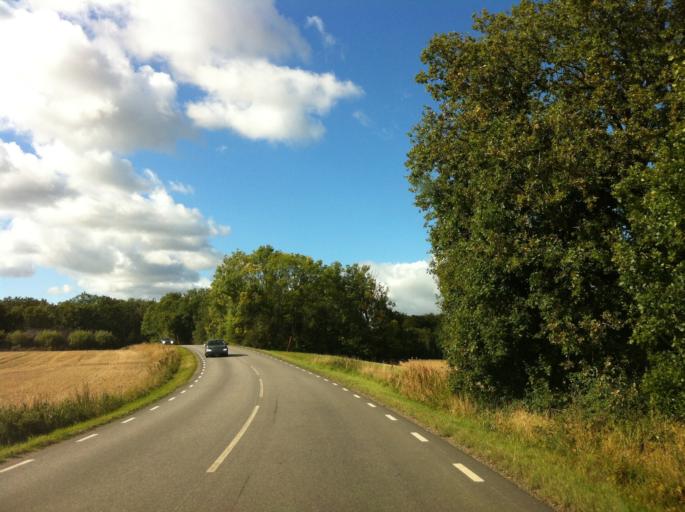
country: SE
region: Skane
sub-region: Tomelilla Kommun
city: Tomelilla
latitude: 55.6504
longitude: 13.9468
